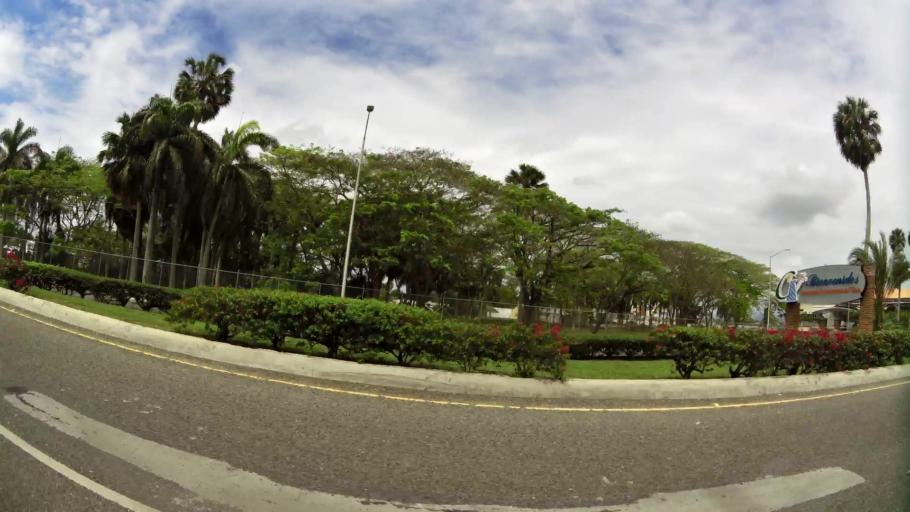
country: DO
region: Santiago
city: Licey al Medio
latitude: 19.4004
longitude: -70.6023
